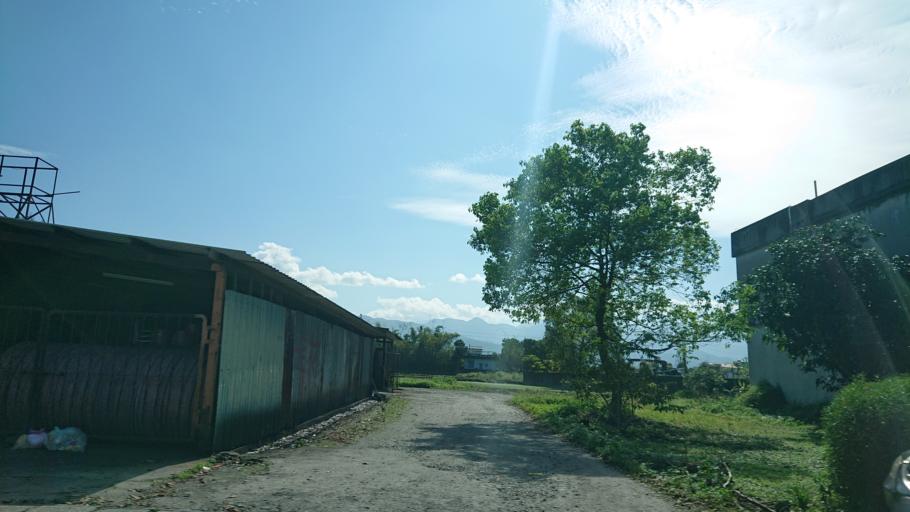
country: TW
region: Taiwan
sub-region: Yilan
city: Yilan
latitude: 24.6698
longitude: 121.7240
